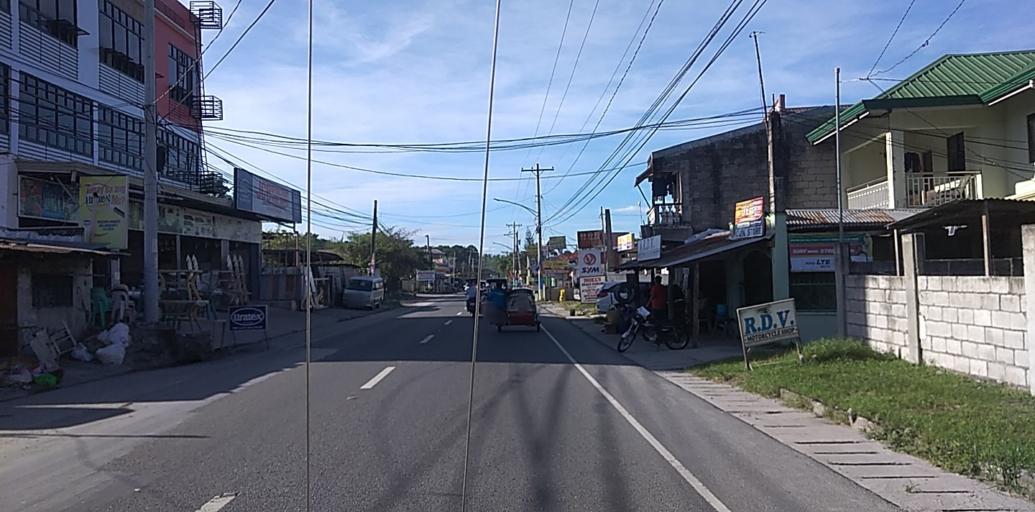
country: PH
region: Central Luzon
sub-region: Province of Pampanga
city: Porac
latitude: 15.0760
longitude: 120.5438
